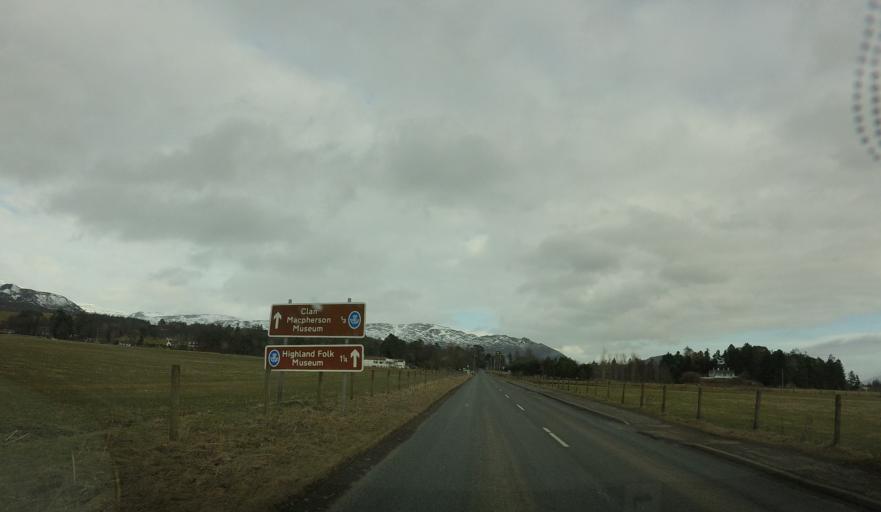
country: GB
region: Scotland
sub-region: Highland
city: Kingussie
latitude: 57.0580
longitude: -4.1295
